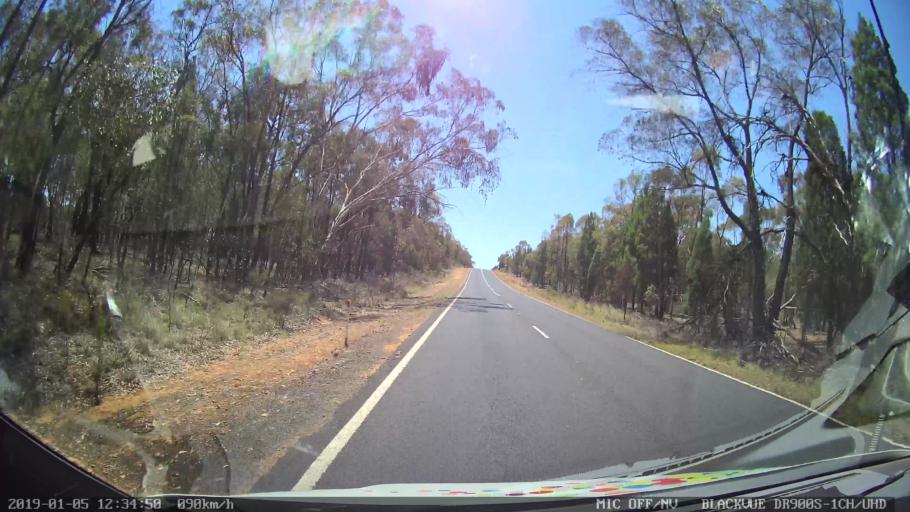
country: AU
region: New South Wales
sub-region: Warrumbungle Shire
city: Coonabarabran
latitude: -31.2111
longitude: 149.4164
